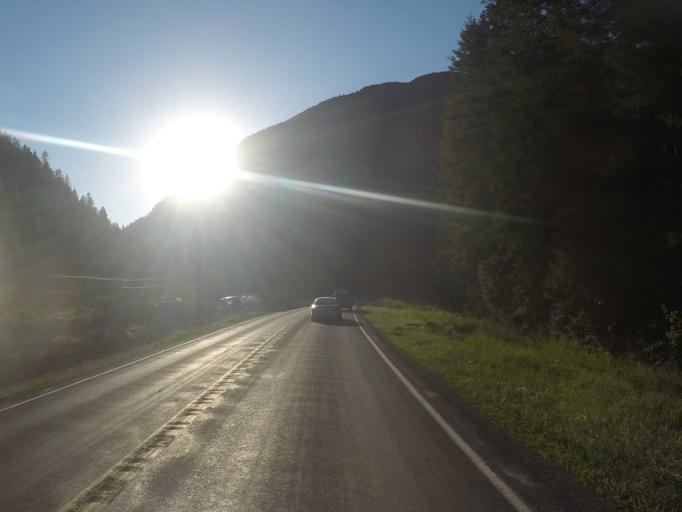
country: US
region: Montana
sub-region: Flathead County
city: Columbia Falls
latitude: 48.3864
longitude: -114.0887
